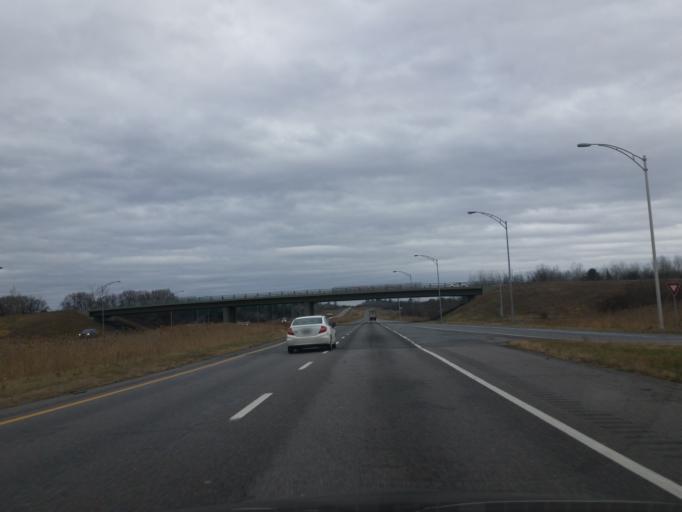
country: CA
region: Quebec
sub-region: Outaouais
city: Val-des-Monts
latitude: 45.5331
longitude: -75.4991
